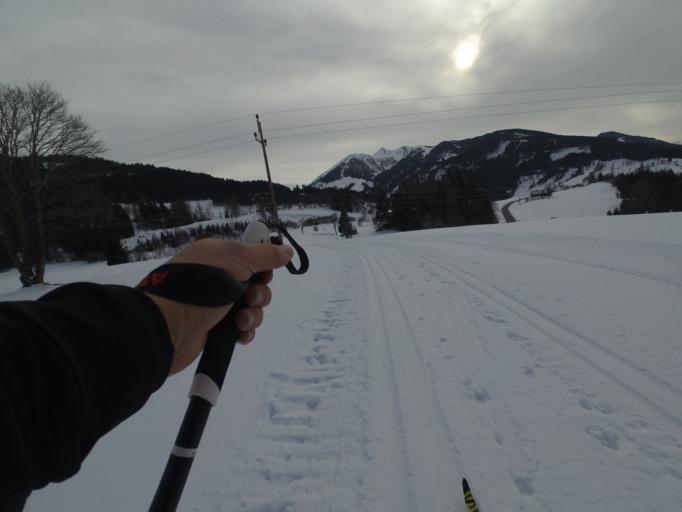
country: AT
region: Salzburg
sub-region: Politischer Bezirk Zell am See
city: Taxenbach
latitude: 47.2867
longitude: 12.9871
